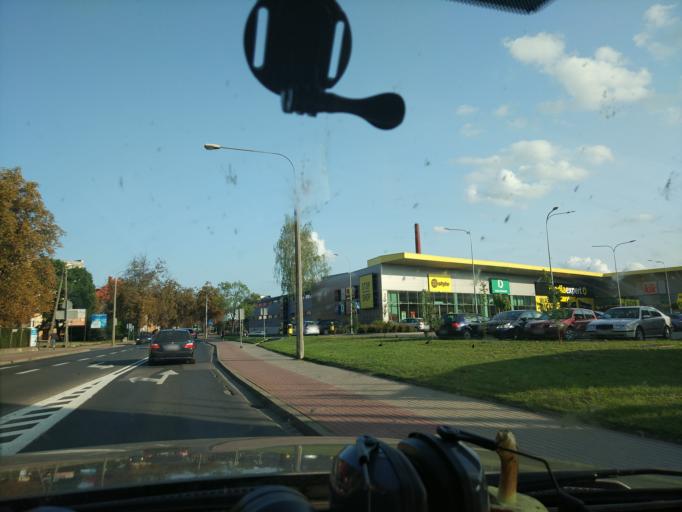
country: PL
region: Warmian-Masurian Voivodeship
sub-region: Powiat szczycienski
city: Szczytno
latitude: 53.5635
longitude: 20.9877
